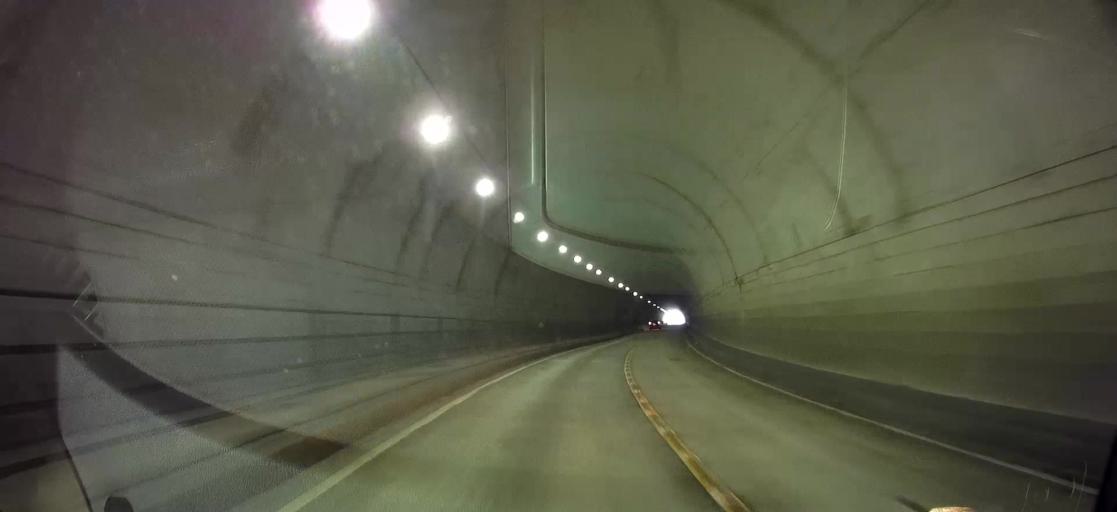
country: JP
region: Kumamoto
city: Hondo
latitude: 32.4325
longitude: 130.4045
